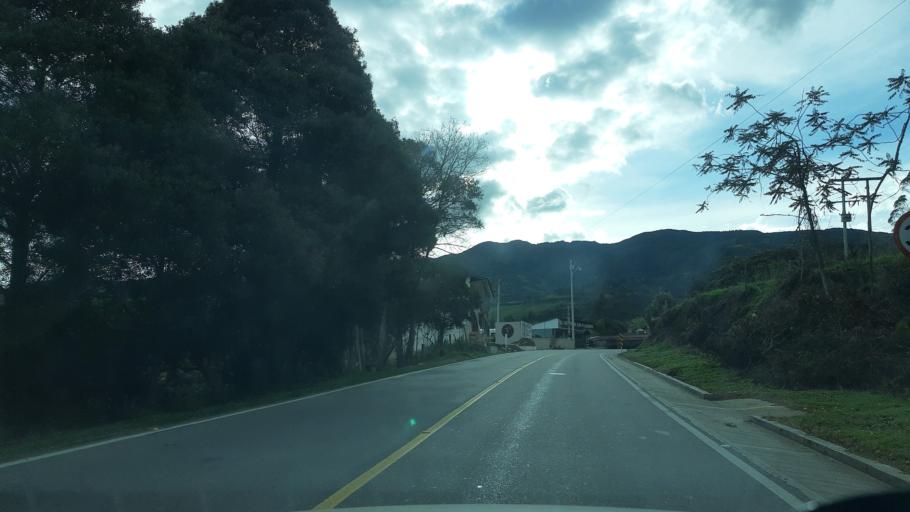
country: CO
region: Cundinamarca
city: Macheta
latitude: 5.0801
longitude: -73.6216
